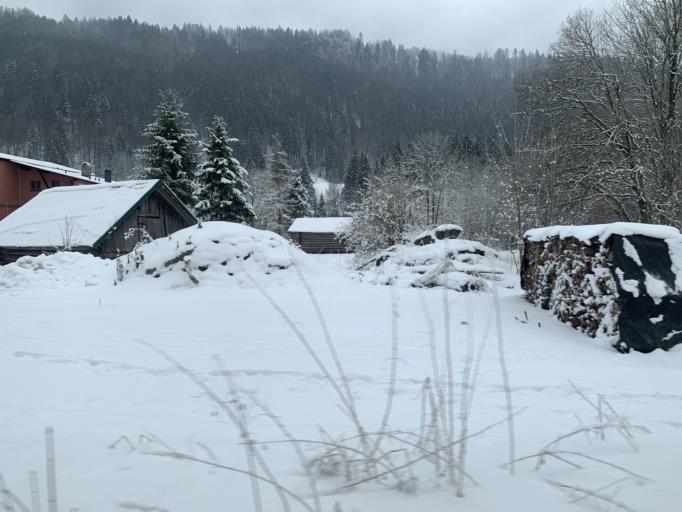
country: DE
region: Bavaria
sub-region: Upper Bavaria
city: Farchant
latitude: 47.4875
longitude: 11.1790
